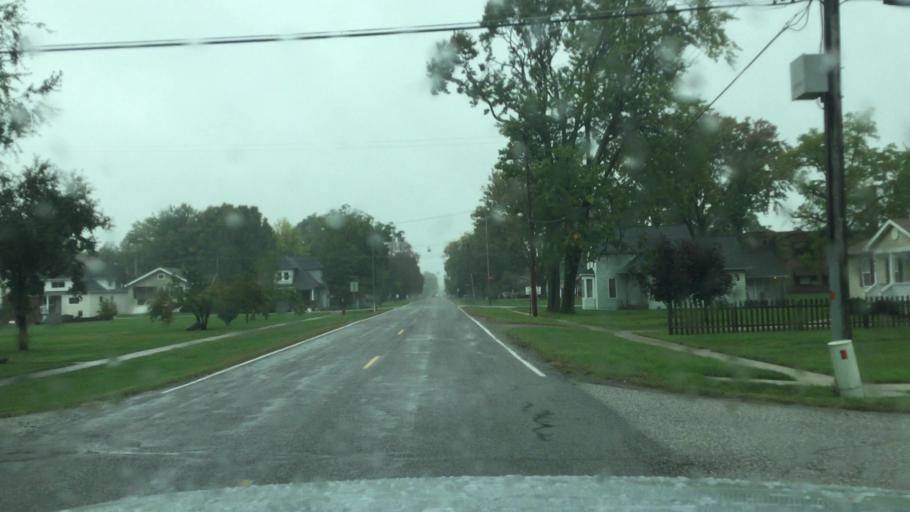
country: US
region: Michigan
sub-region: Saginaw County
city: Carrollton
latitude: 43.4576
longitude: -83.9301
